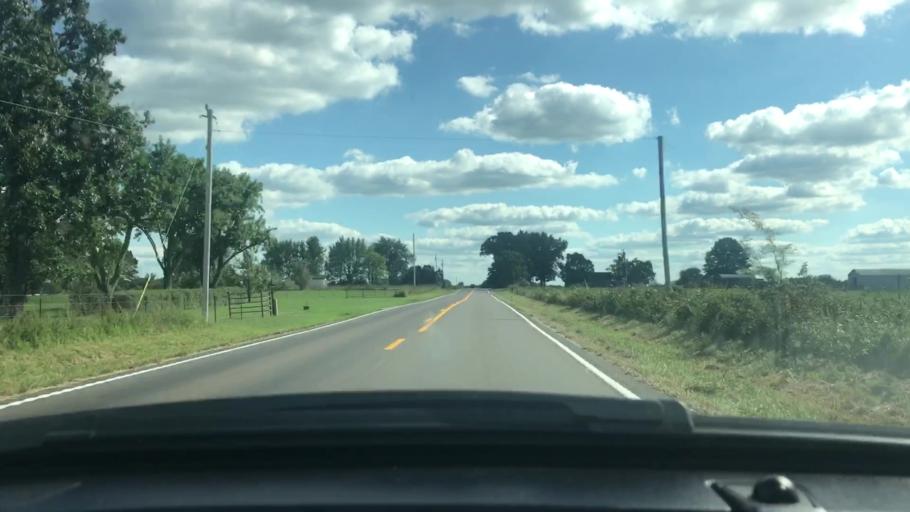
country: US
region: Missouri
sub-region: Wright County
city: Mountain Grove
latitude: 37.2647
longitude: -92.3081
